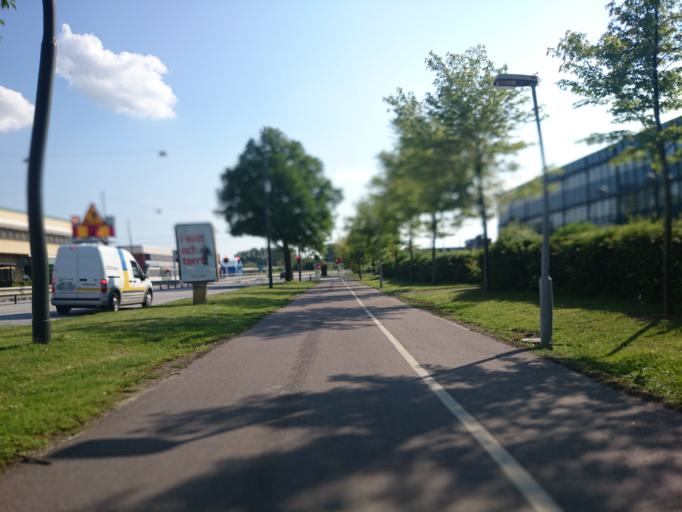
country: SE
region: Skane
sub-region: Burlovs Kommun
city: Arloev
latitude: 55.6248
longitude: 13.0623
